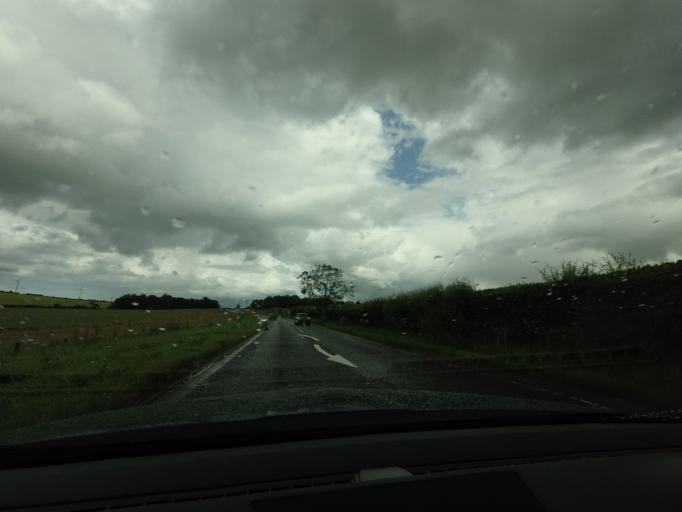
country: GB
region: Scotland
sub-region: Aberdeenshire
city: Turriff
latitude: 57.5466
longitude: -2.4438
